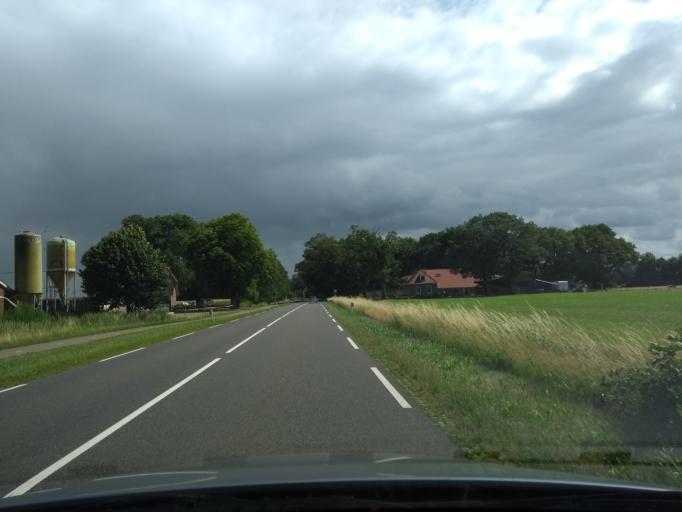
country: NL
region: Overijssel
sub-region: Gemeente Twenterand
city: Den Ham
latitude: 52.4378
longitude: 6.4361
